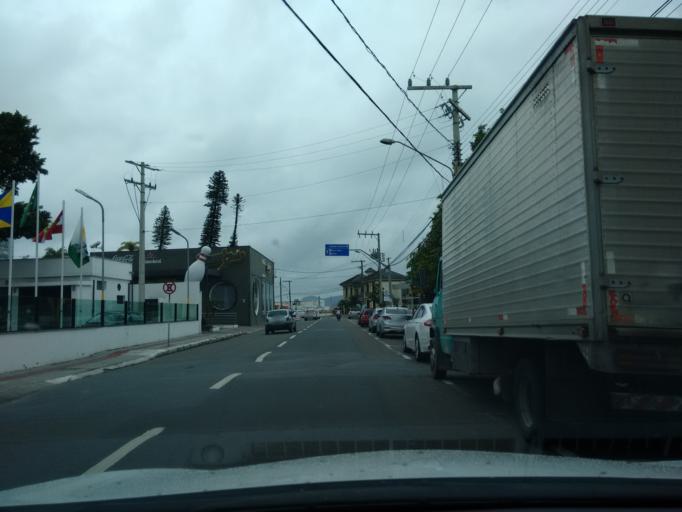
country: BR
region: Santa Catarina
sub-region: Navegantes
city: Navegantes
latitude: -26.9057
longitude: -48.6543
